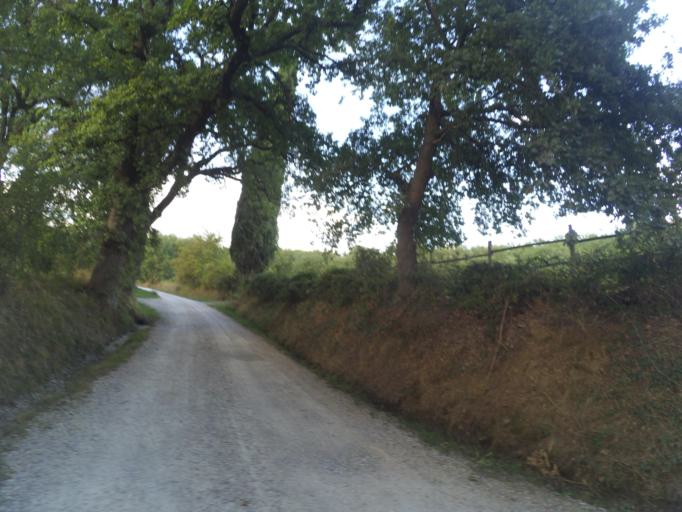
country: IT
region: Tuscany
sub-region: Province of Arezzo
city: Castiglion Fibocchi
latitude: 43.5330
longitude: 11.7657
